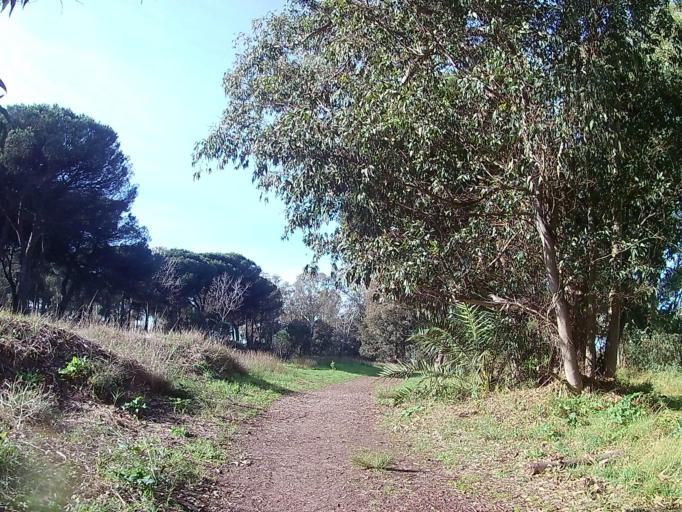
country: IT
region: Latium
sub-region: Citta metropolitana di Roma Capitale
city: Lido di Ostia
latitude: 41.7449
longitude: 12.2730
